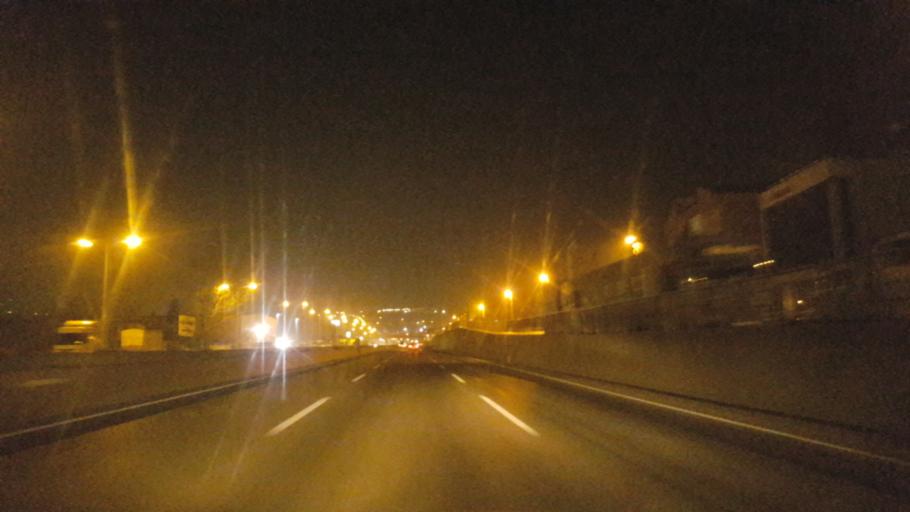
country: TR
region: Kocaeli
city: Tavsancil
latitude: 40.7841
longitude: 29.5366
